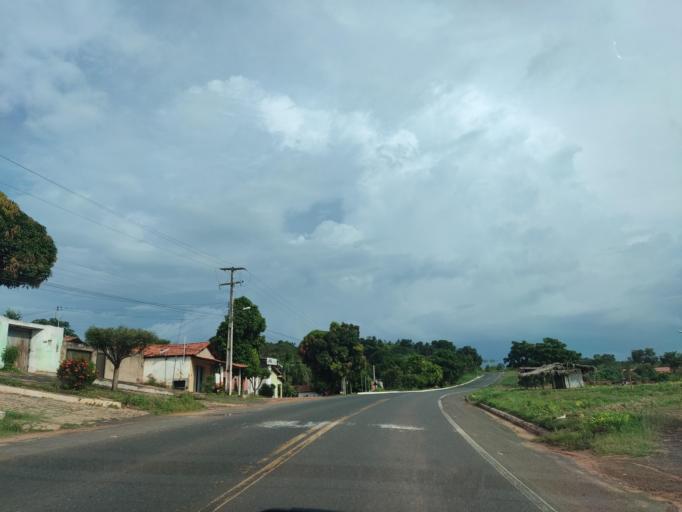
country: BR
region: Piaui
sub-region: Agua Branca
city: Agua Branca
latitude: -5.8221
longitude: -42.5068
